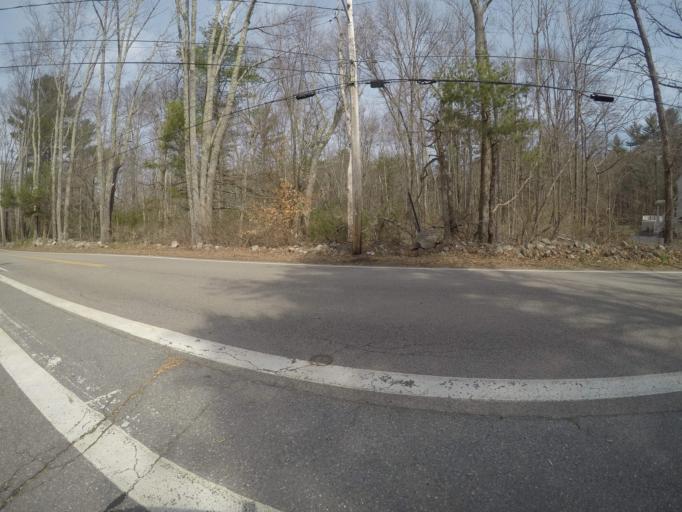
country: US
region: Massachusetts
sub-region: Bristol County
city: Easton
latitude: 42.0520
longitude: -71.1176
